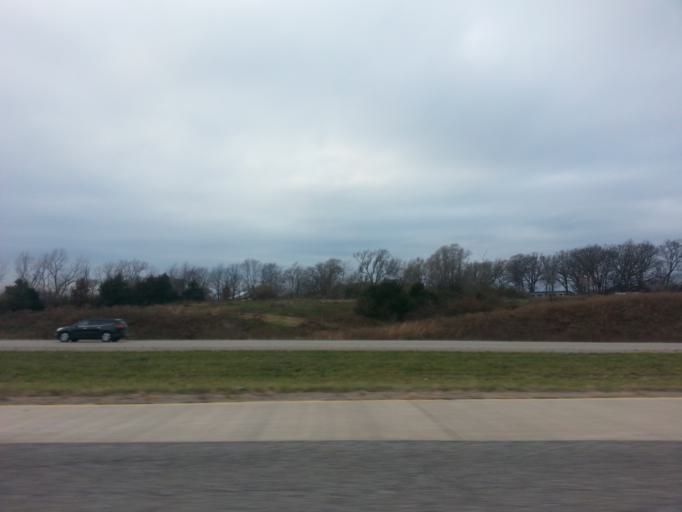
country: US
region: Iowa
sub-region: Henry County
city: Mount Pleasant
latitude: 40.9107
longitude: -91.5472
